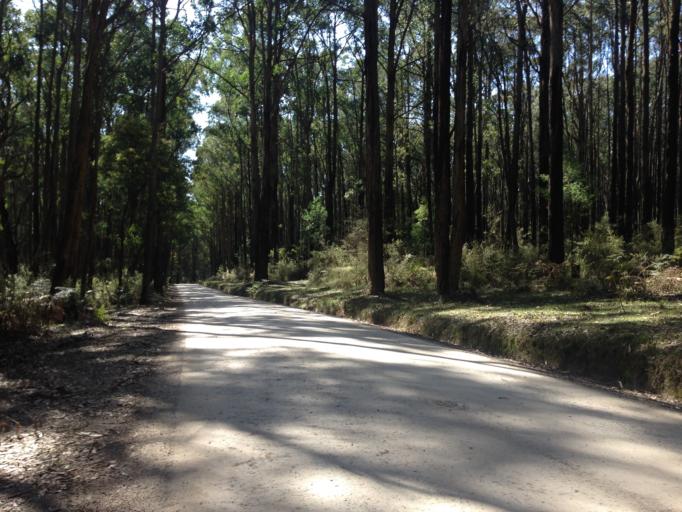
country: AU
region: Victoria
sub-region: Yarra Ranges
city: Mount Dandenong
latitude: -37.8362
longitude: 145.3978
